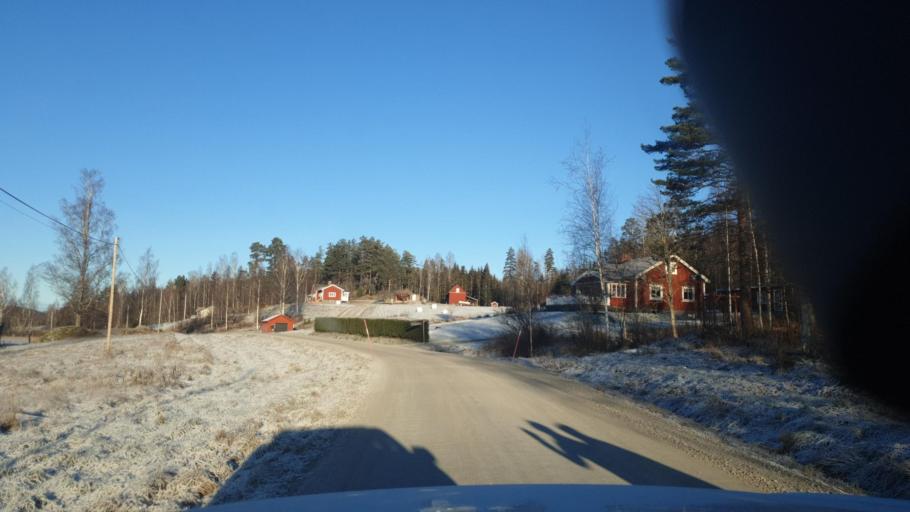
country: SE
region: Vaermland
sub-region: Arvika Kommun
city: Arvika
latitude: 59.7221
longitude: 12.8373
